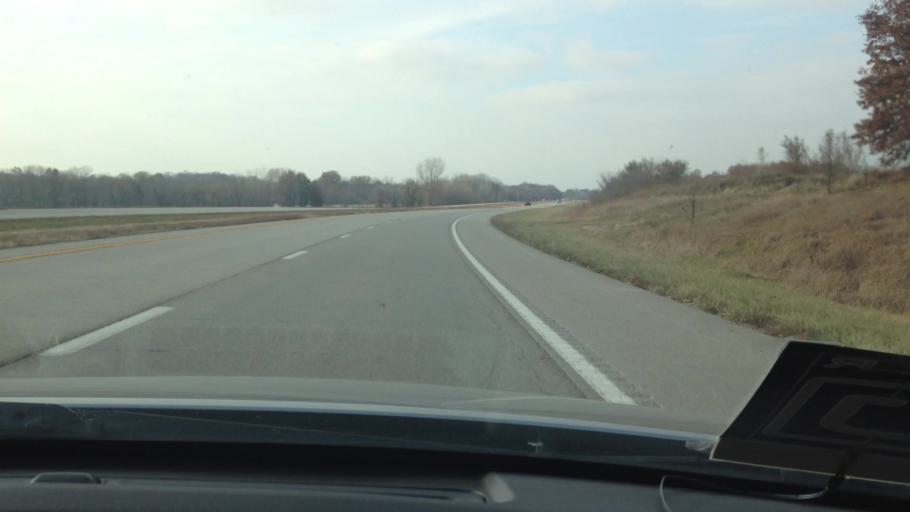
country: US
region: Missouri
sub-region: Cass County
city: Garden City
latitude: 38.5070
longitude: -94.0943
